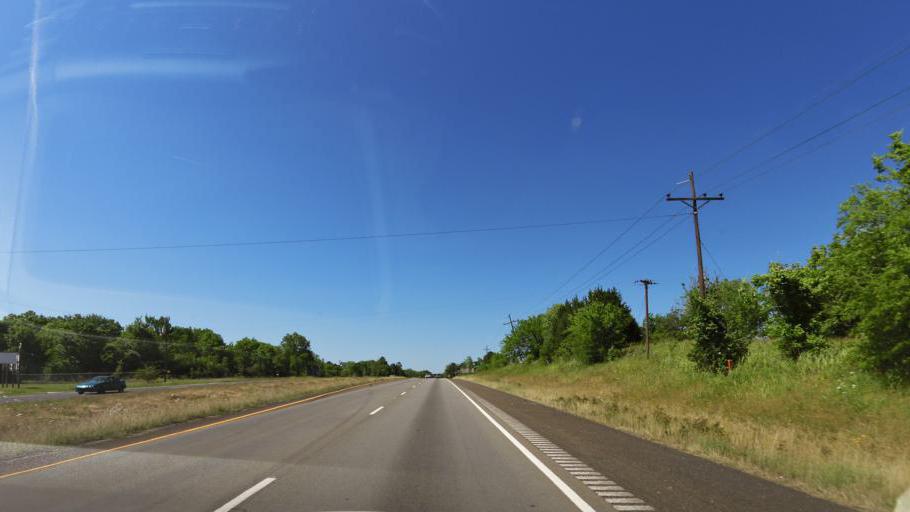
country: US
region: Texas
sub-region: San Jacinto County
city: Shepherd
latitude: 30.5913
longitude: -94.9446
